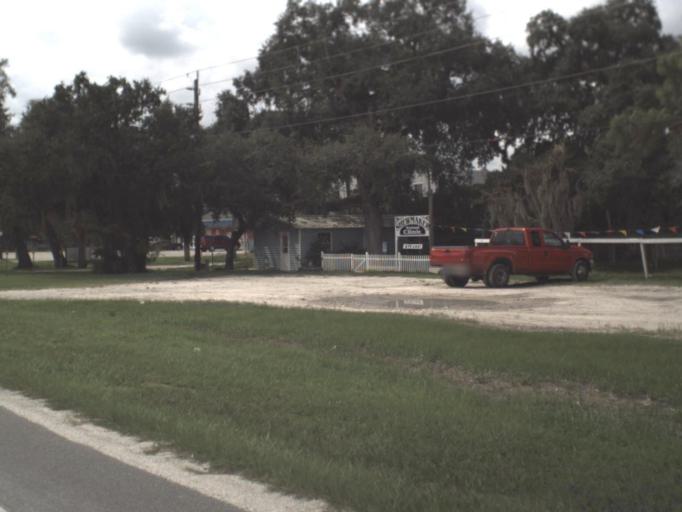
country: US
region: Florida
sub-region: Hendry County
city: LaBelle
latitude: 26.7774
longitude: -81.4375
